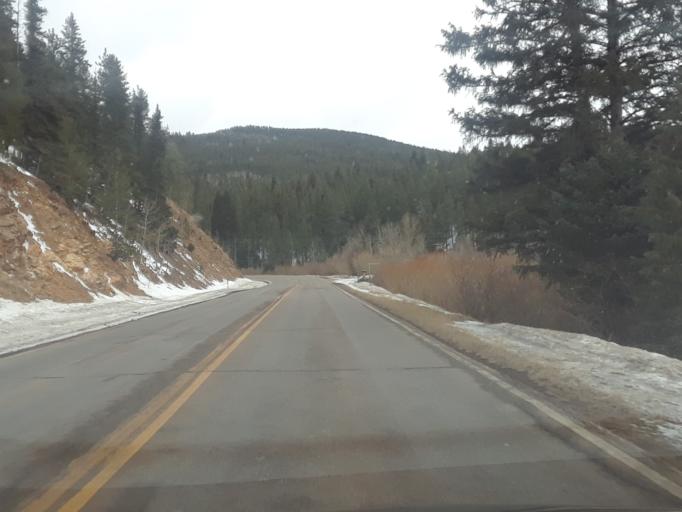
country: US
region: Colorado
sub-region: Boulder County
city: Coal Creek
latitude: 39.8267
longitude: -105.4103
